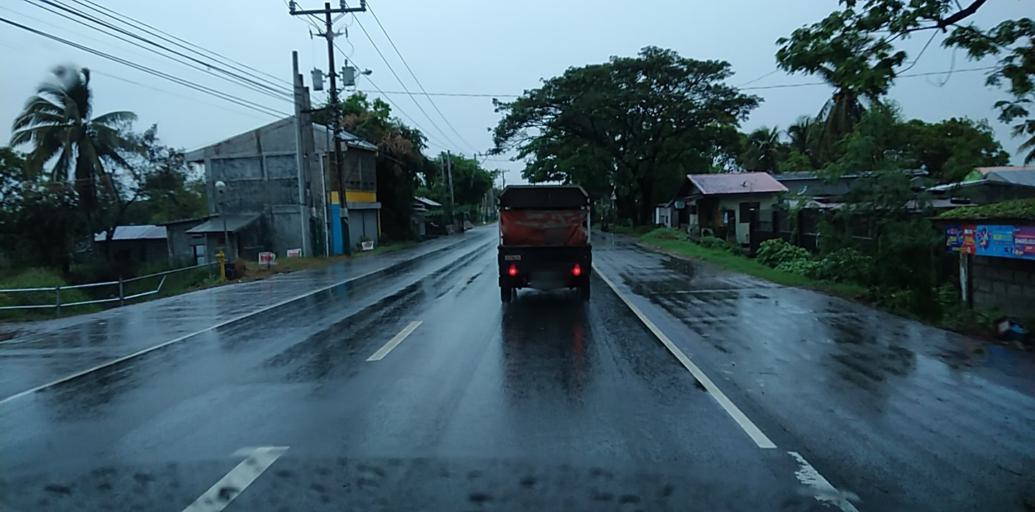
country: PH
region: Central Luzon
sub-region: Province of Bulacan
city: Bulualto
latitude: 15.2184
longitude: 120.9545
